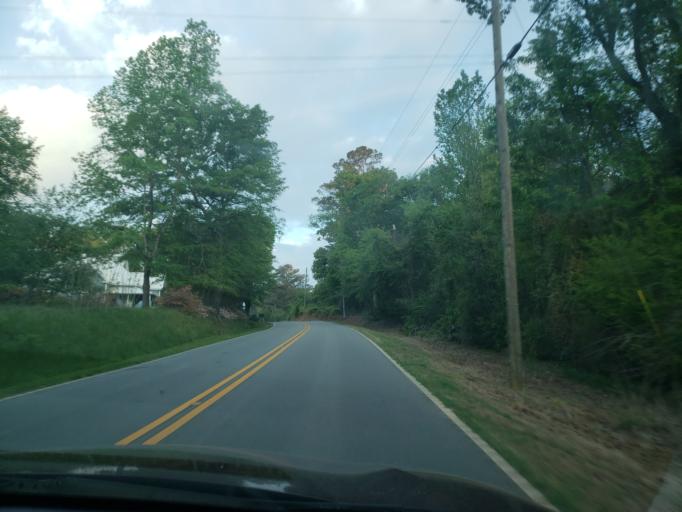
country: US
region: Alabama
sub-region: Tallapoosa County
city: Dadeville
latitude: 32.7024
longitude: -85.7510
